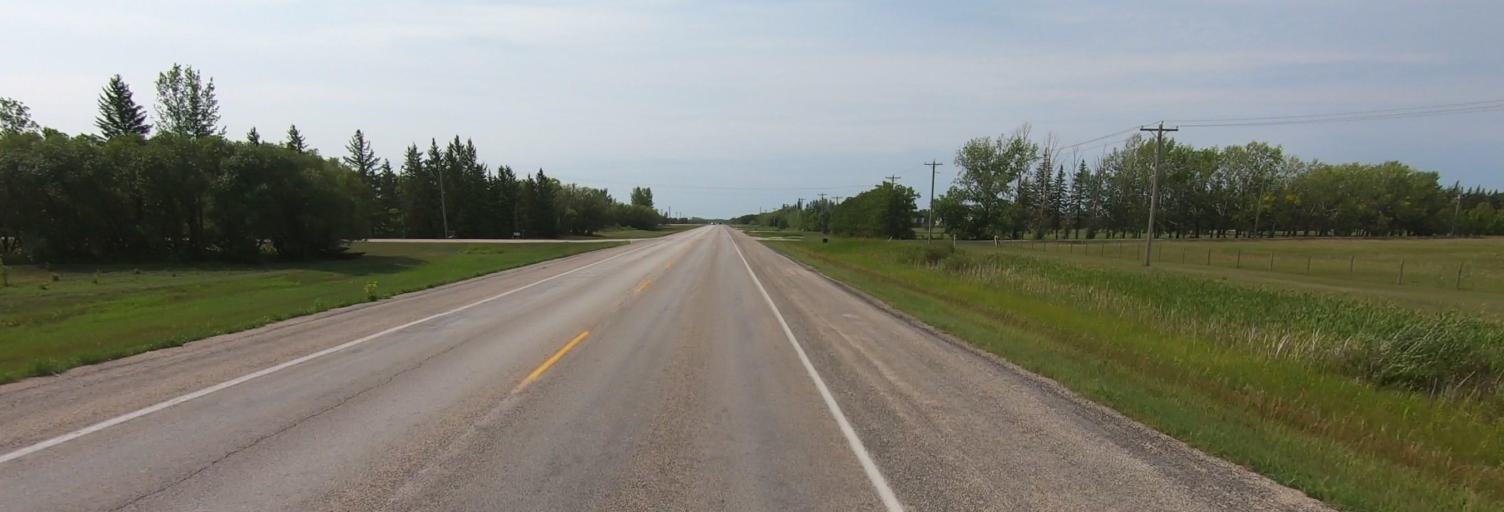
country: CA
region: Manitoba
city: Niverville
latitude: 49.6250
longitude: -97.1147
